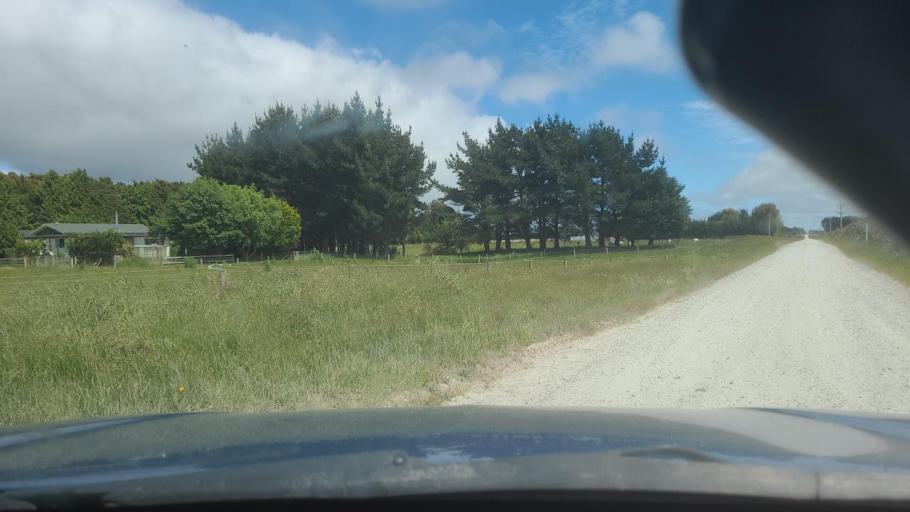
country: NZ
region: Southland
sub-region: Invercargill City
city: Invercargill
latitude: -46.4662
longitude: 168.5061
